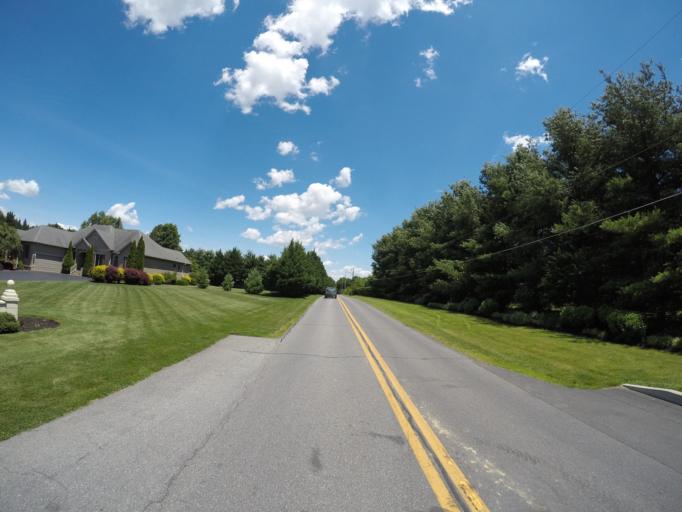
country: US
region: Delaware
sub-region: New Castle County
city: Middletown
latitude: 39.4810
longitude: -75.7693
